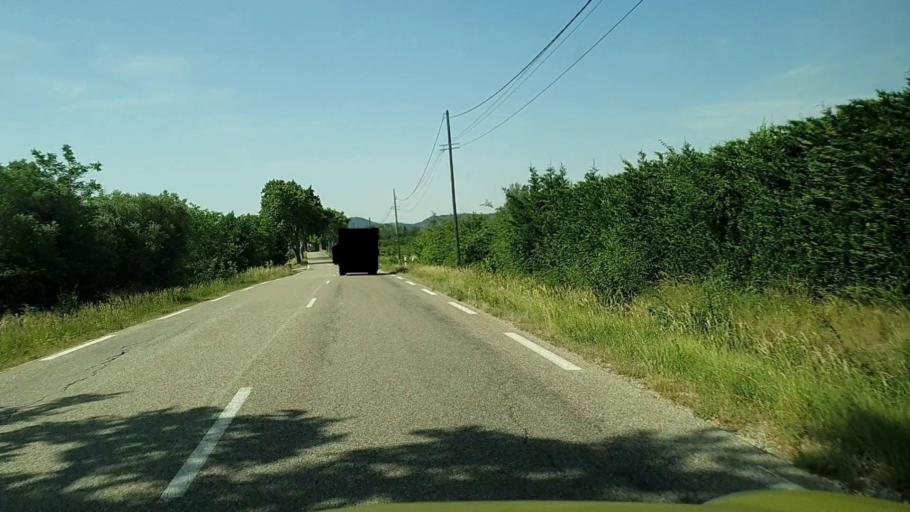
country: FR
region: Languedoc-Roussillon
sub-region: Departement du Gard
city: Castillon-du-Gard
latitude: 43.9659
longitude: 4.5722
